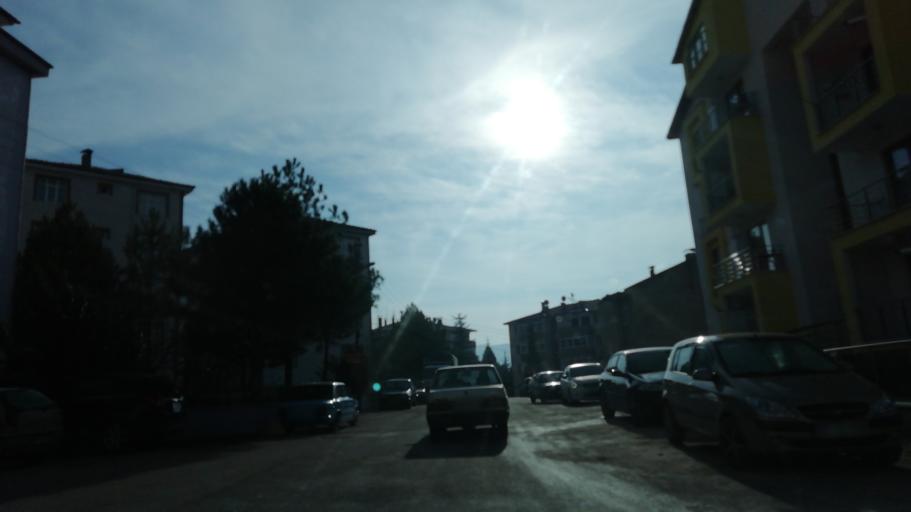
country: TR
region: Karabuk
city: Safranbolu
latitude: 41.2535
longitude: 32.6722
